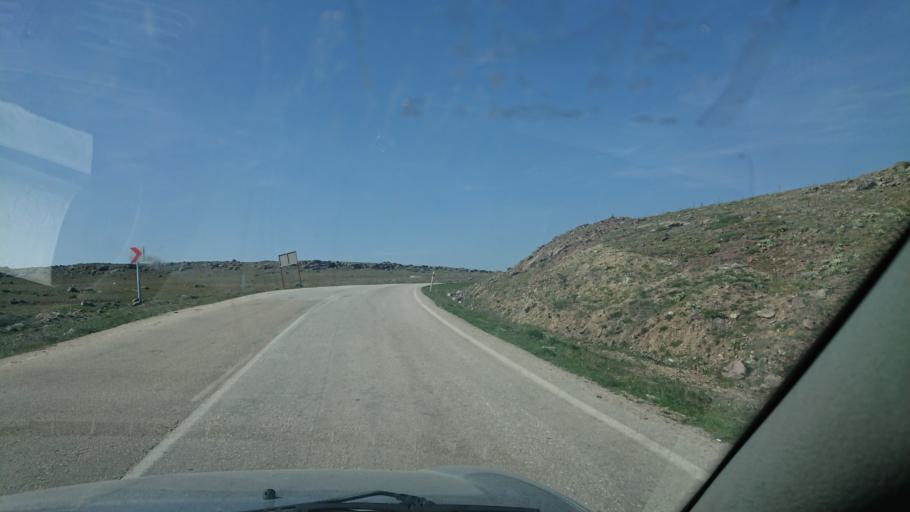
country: TR
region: Eskisehir
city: Eskisehir
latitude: 39.6817
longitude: 30.4858
